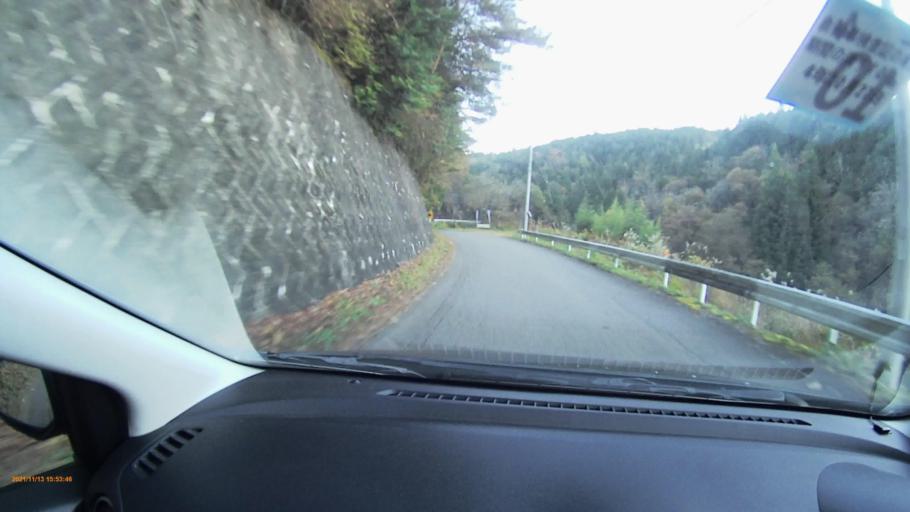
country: JP
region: Gifu
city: Nakatsugawa
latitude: 35.5956
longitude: 137.4406
